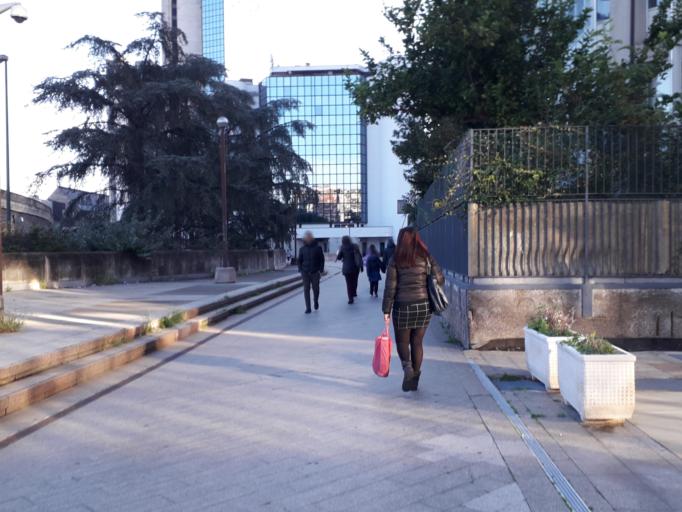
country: IT
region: Campania
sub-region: Provincia di Napoli
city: Napoli
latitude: 40.8582
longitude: 14.2779
